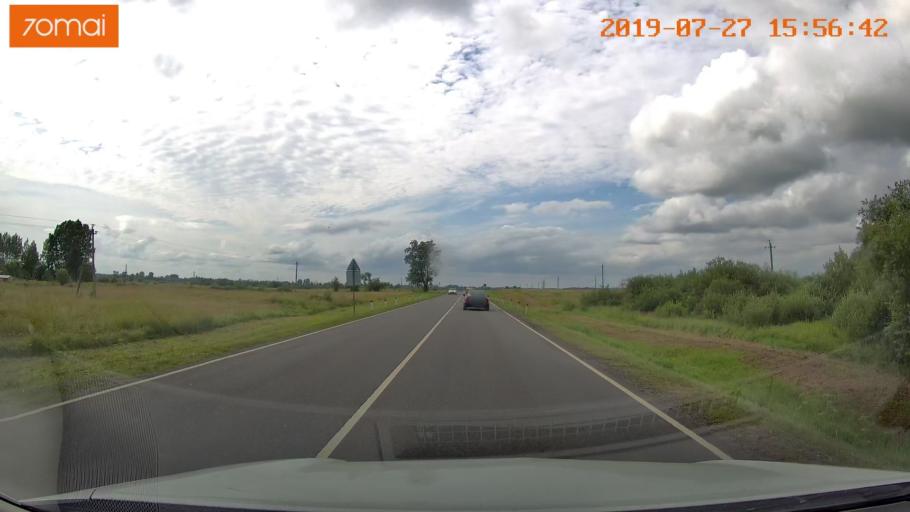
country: RU
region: Kaliningrad
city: Chernyakhovsk
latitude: 54.6208
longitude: 21.8972
